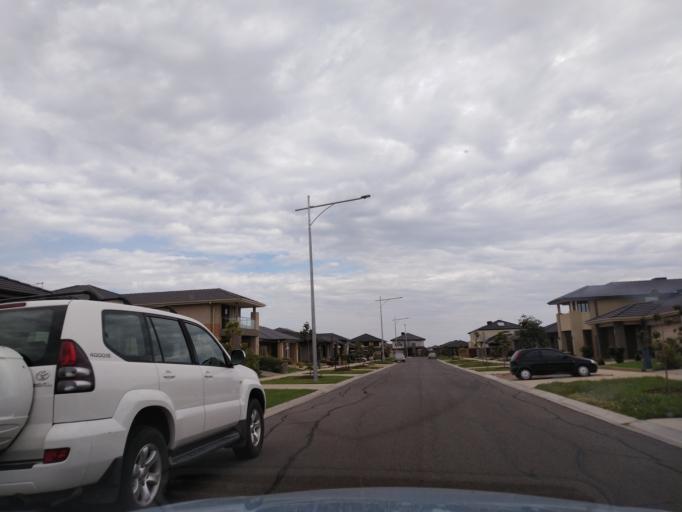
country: AU
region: Victoria
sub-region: Wyndham
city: Williams Landing
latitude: -37.8384
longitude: 144.7137
